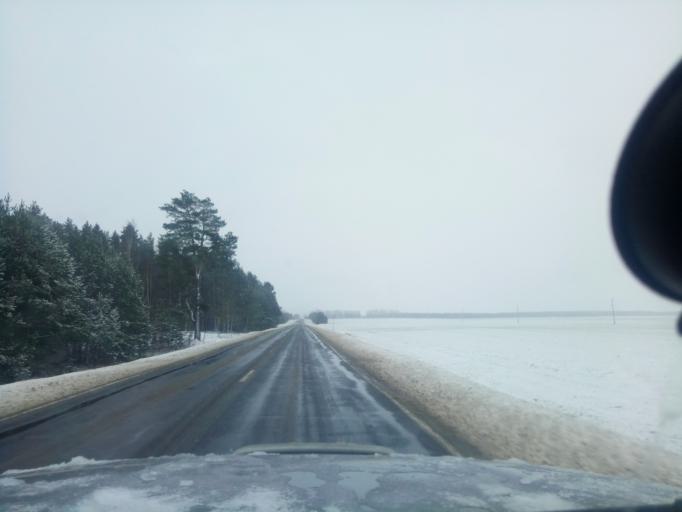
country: BY
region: Minsk
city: Haradzyeya
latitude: 53.3713
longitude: 26.5108
